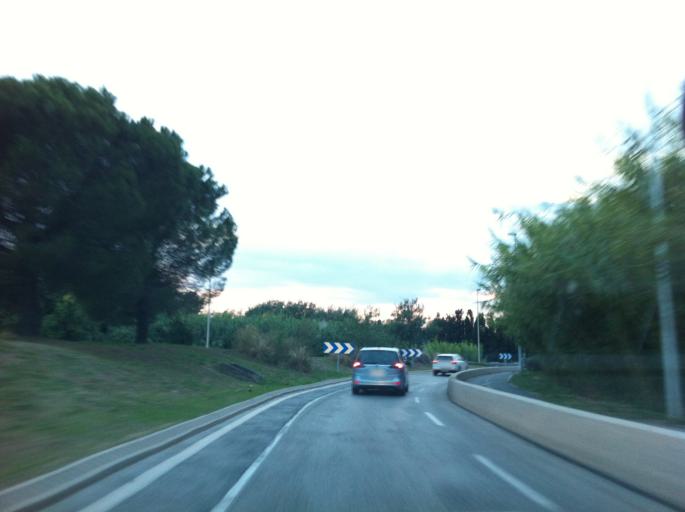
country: FR
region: Provence-Alpes-Cote d'Azur
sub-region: Departement du Var
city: Gassin
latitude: 43.2597
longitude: 6.5921
